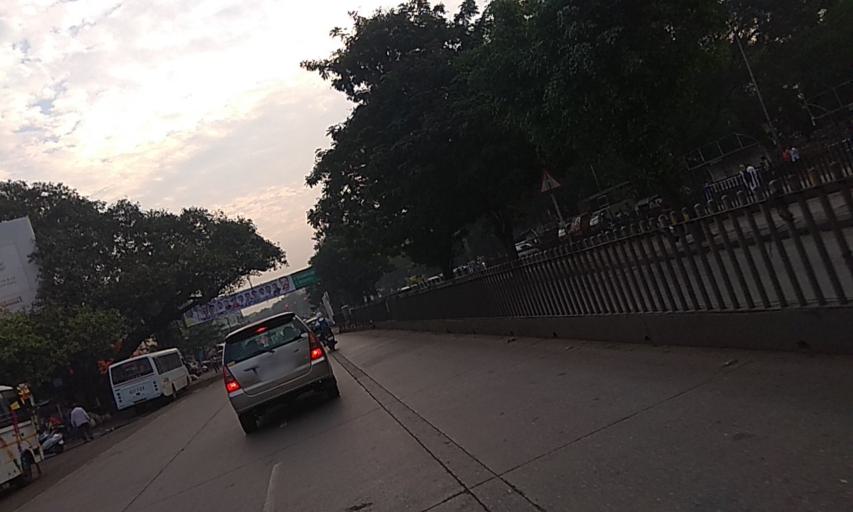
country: IN
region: Maharashtra
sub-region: Pune Division
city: Shivaji Nagar
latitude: 18.5454
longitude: 73.8865
